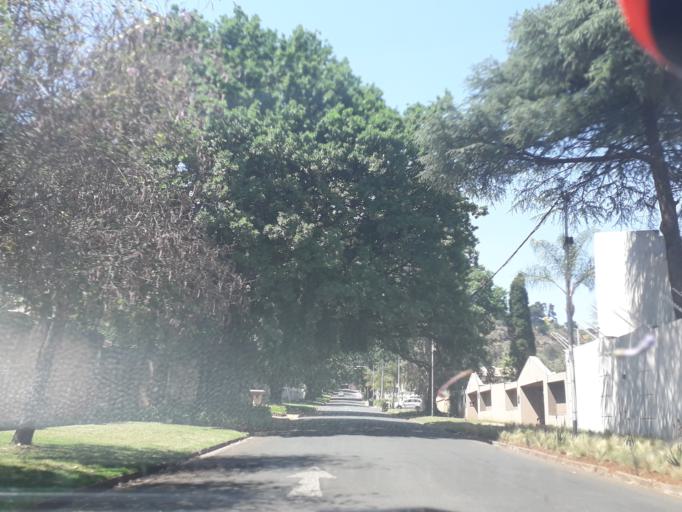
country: ZA
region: Gauteng
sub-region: City of Johannesburg Metropolitan Municipality
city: Johannesburg
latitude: -26.1678
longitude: 28.0583
